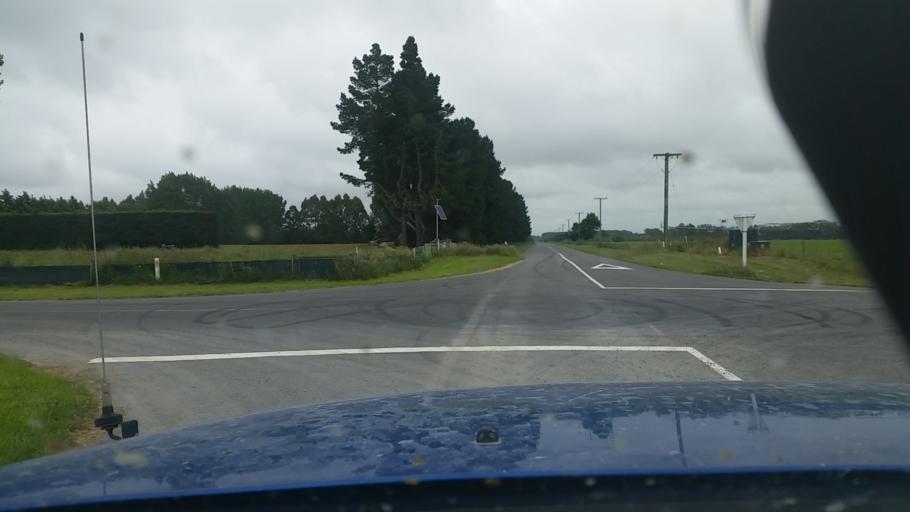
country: NZ
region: Canterbury
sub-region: Ashburton District
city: Ashburton
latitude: -43.8609
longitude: 171.7728
